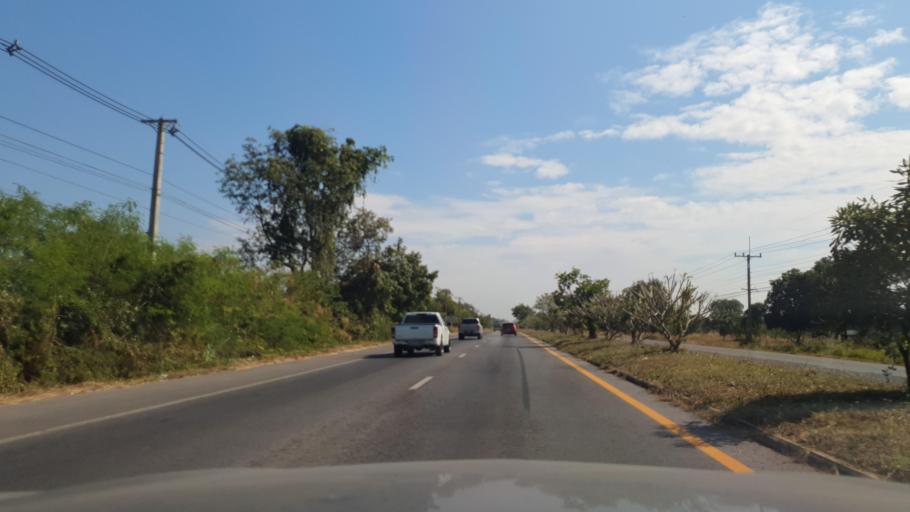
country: TH
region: Maha Sarakham
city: Chiang Yuen
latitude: 16.3804
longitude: 103.1996
